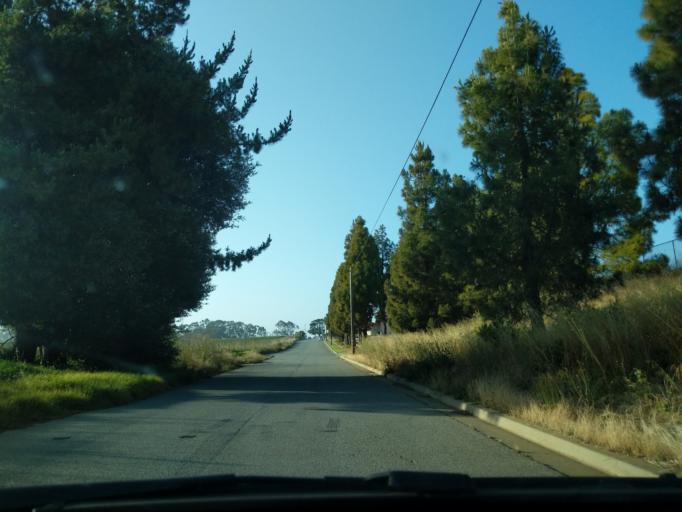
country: US
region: California
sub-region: Monterey County
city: Las Lomas
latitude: 36.8681
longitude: -121.7624
